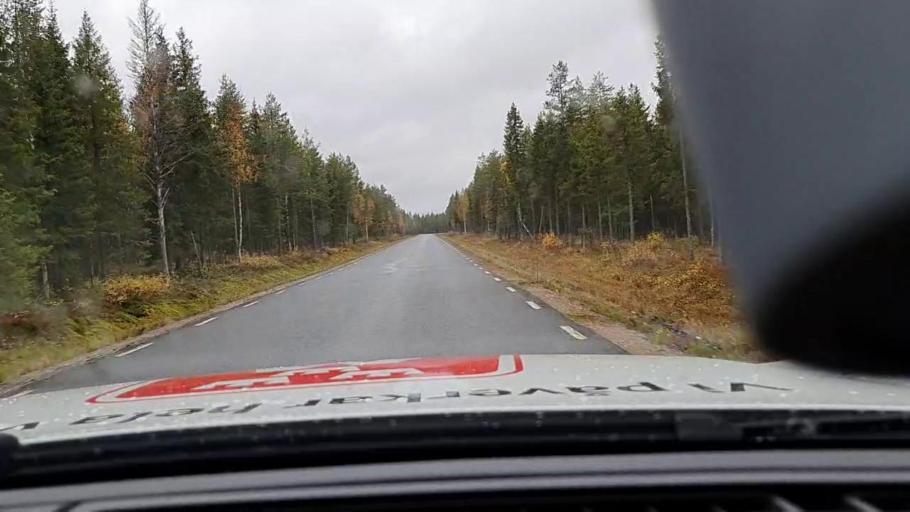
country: SE
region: Norrbotten
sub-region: Haparanda Kommun
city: Haparanda
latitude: 65.9366
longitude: 23.8090
